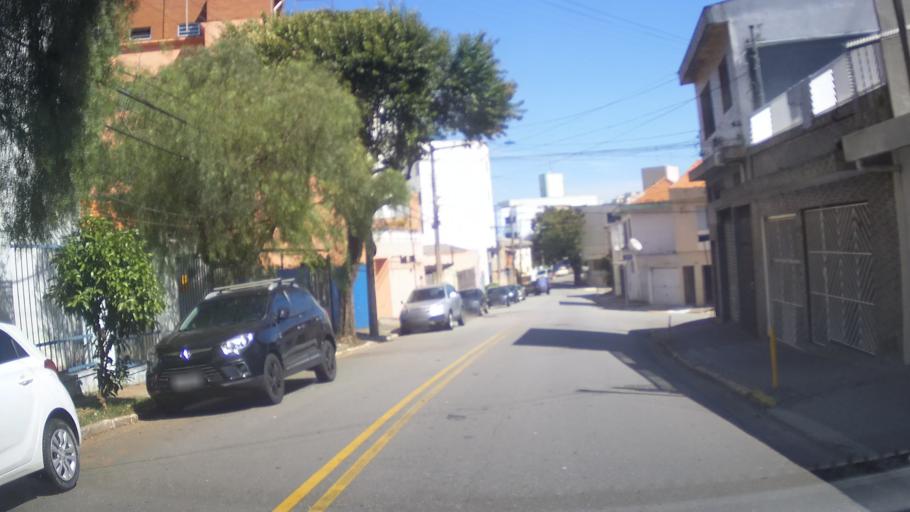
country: BR
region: Sao Paulo
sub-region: Sao Caetano Do Sul
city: Sao Caetano do Sul
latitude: -23.6359
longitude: -46.5712
